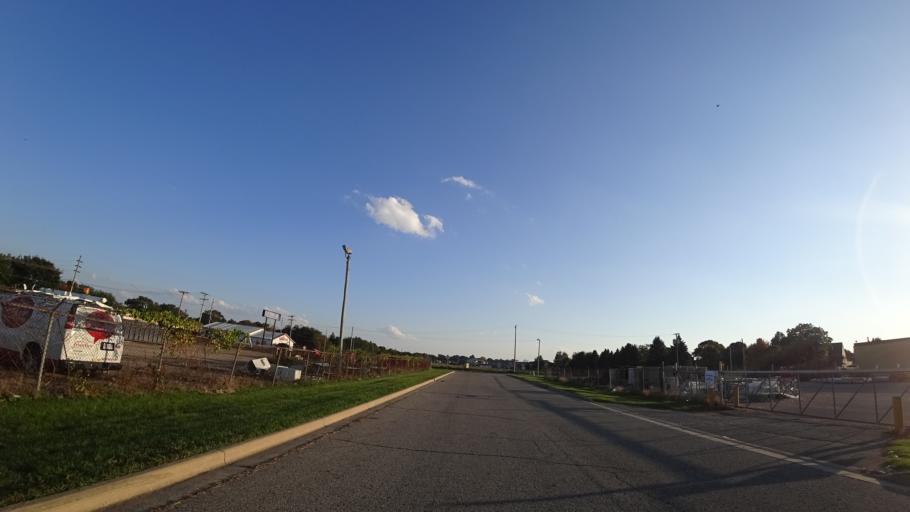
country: US
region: Michigan
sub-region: Saint Joseph County
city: Three Rivers
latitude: 41.9499
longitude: -85.6470
